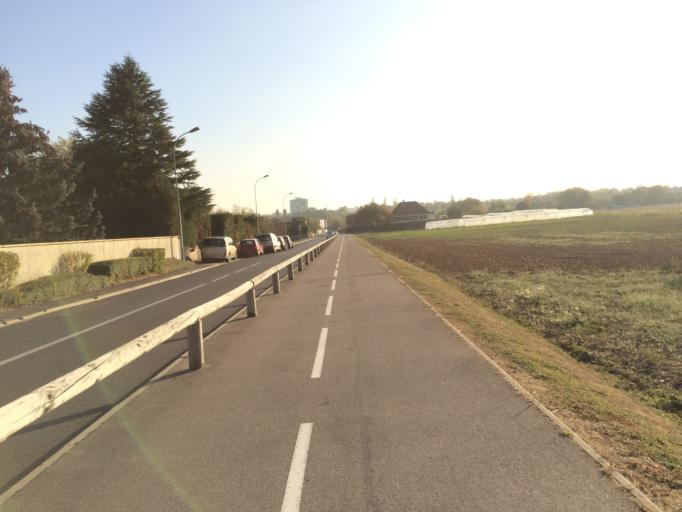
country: FR
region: Ile-de-France
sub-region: Departement de l'Essonne
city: Villejust
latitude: 48.6781
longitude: 2.2398
